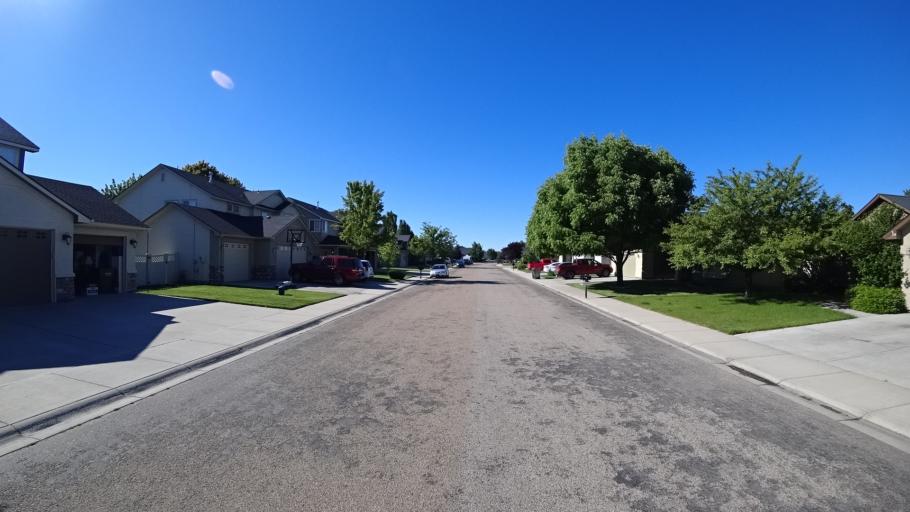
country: US
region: Idaho
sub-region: Ada County
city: Meridian
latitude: 43.6539
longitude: -116.4303
